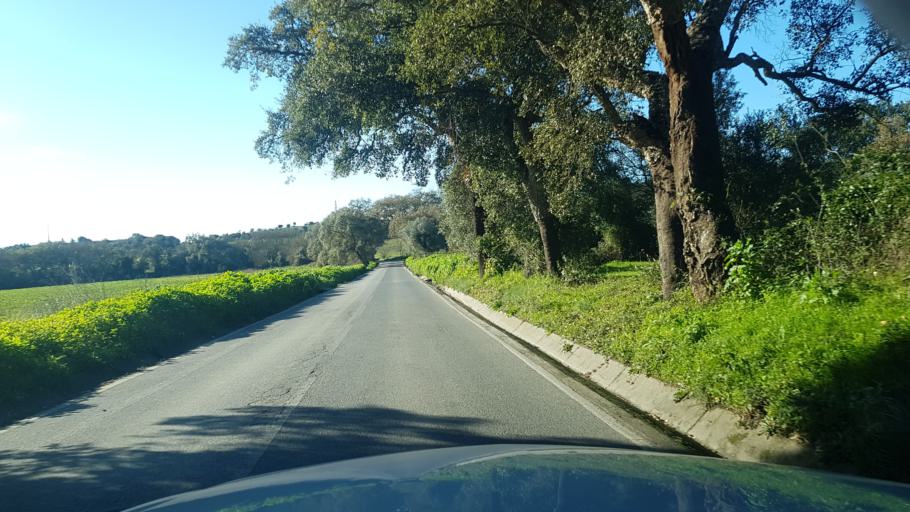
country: PT
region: Santarem
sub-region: Torres Novas
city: Torres Novas
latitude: 39.4757
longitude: -8.5174
